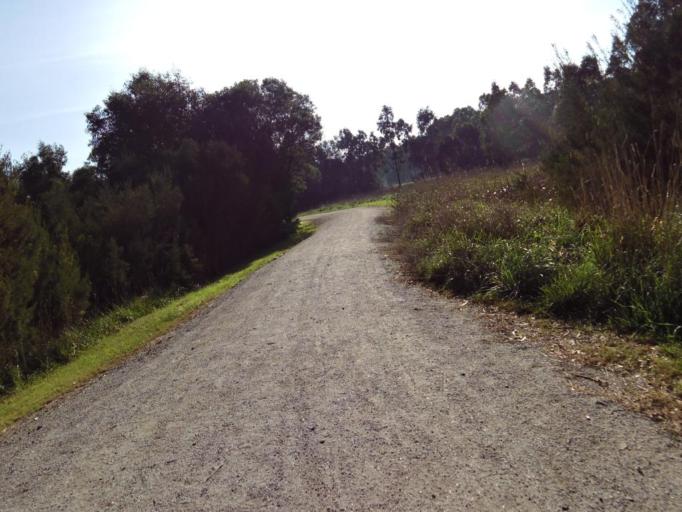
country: AU
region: Victoria
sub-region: Kingston
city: Waterways
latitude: -37.9987
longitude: 145.1249
